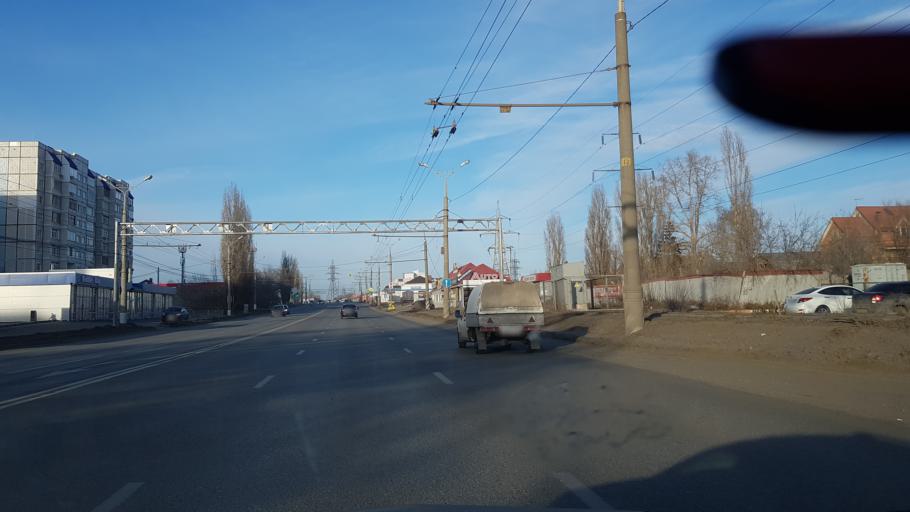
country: RU
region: Samara
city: Tol'yatti
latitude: 53.5317
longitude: 49.3965
